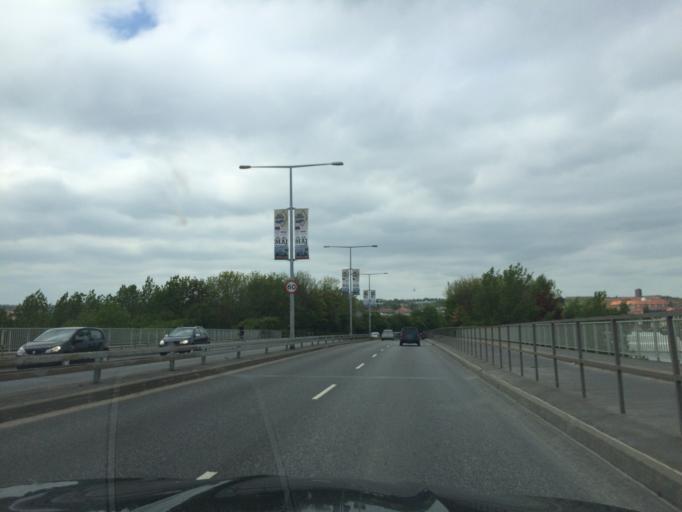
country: DK
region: Central Jutland
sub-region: Arhus Kommune
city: Arhus
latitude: 56.1481
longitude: 10.1850
